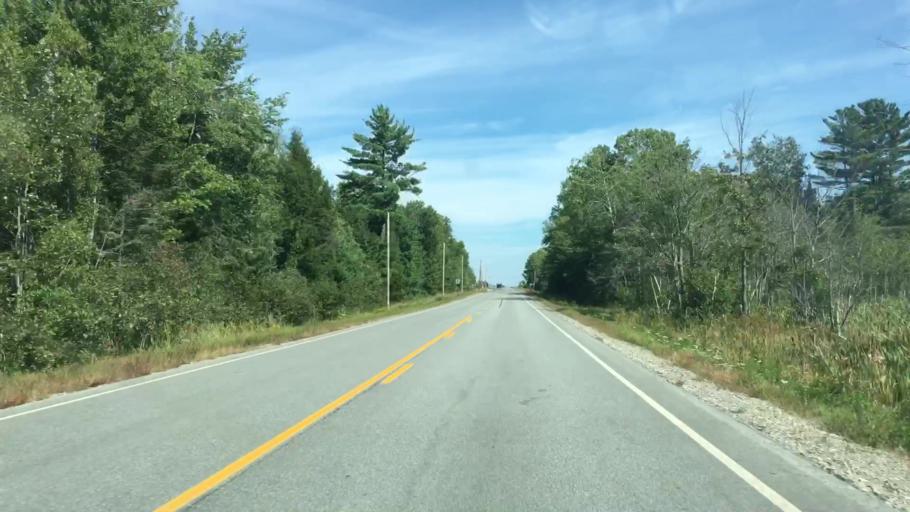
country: US
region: Maine
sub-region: Penobscot County
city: Howland
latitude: 45.2343
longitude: -68.6861
